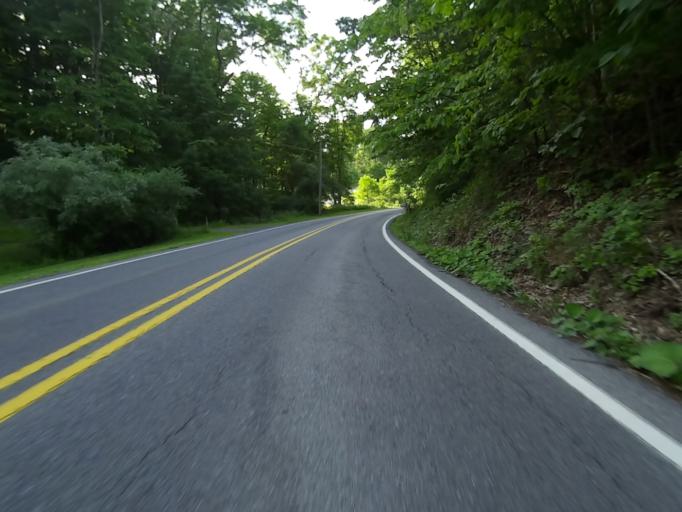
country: US
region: Pennsylvania
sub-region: Centre County
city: Park Forest Village
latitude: 40.8098
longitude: -77.9536
